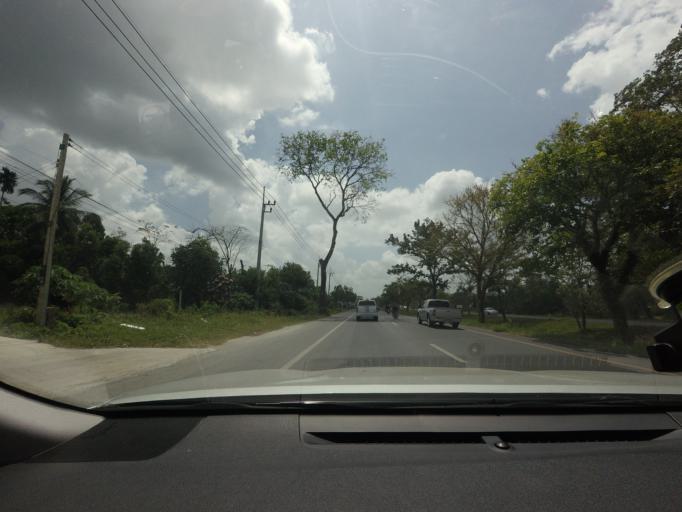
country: TH
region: Nakhon Si Thammarat
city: Nakhon Si Thammarat
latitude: 8.4232
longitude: 99.9215
